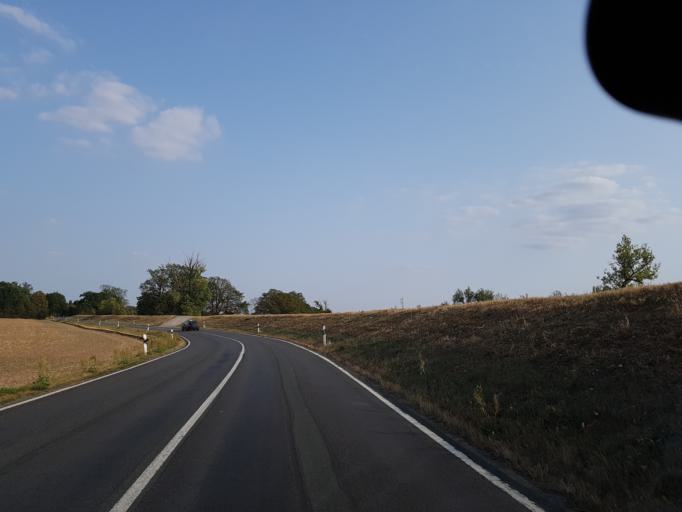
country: DE
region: Saxony
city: Beilrode
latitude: 51.5511
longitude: 13.0439
